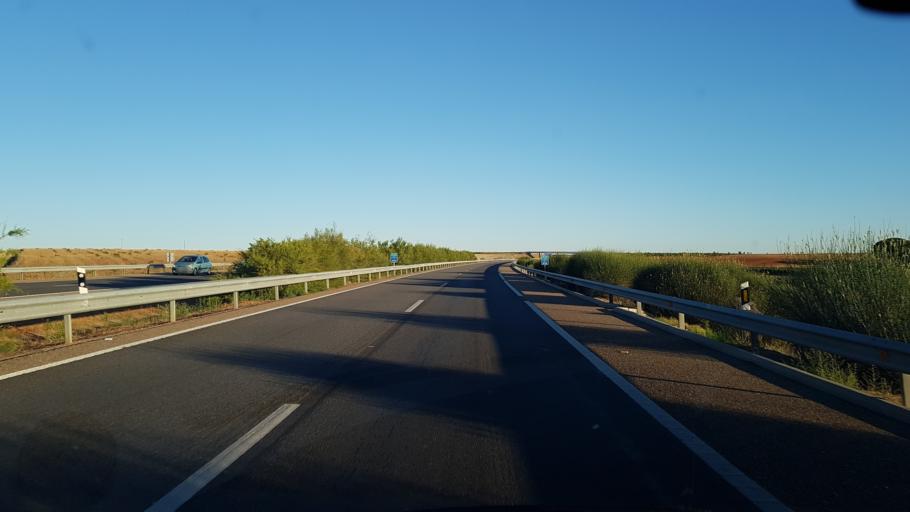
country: ES
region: Castille and Leon
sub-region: Provincia de Zamora
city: Morales de Toro
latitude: 41.5302
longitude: -5.2769
